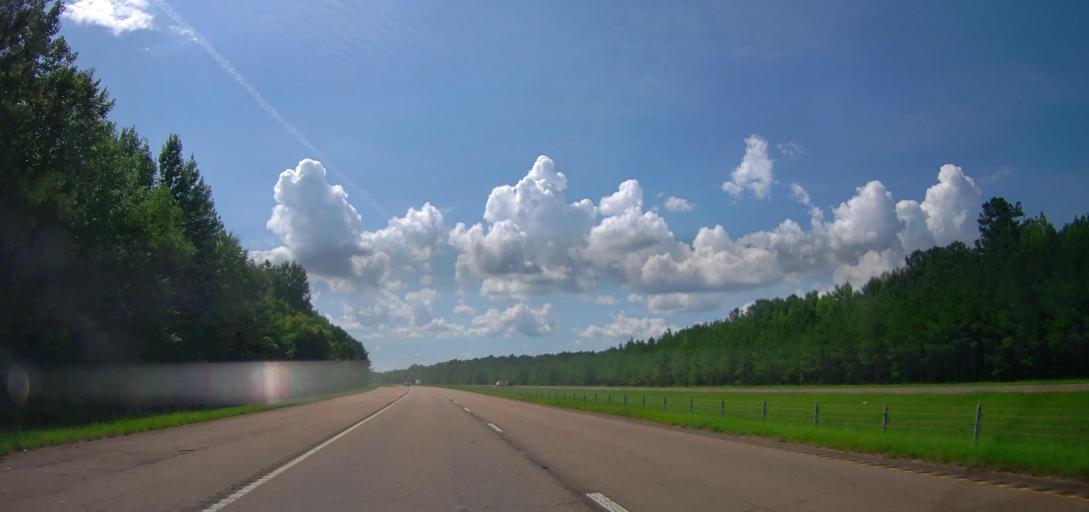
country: US
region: Mississippi
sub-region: Lowndes County
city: New Hope
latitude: 33.5061
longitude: -88.3164
